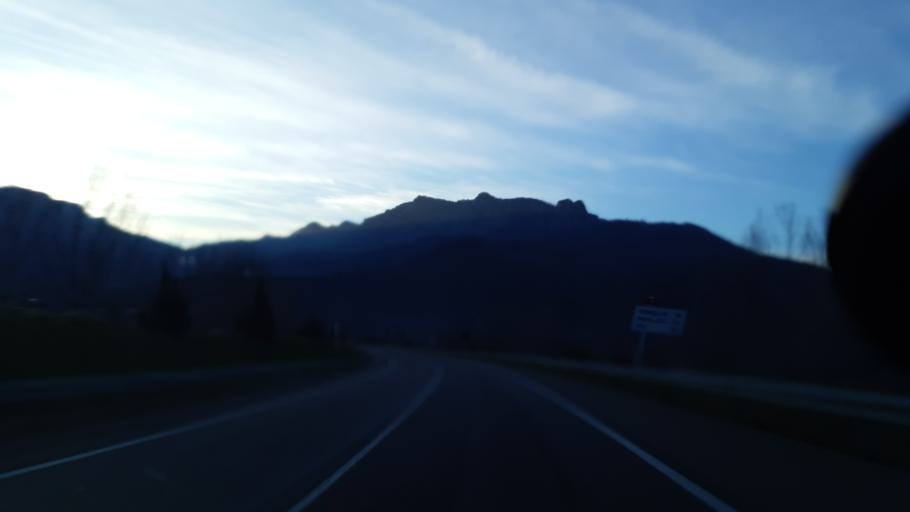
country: ES
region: Catalonia
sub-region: Provincia de Girona
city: Bas
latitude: 42.1290
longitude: 2.4457
